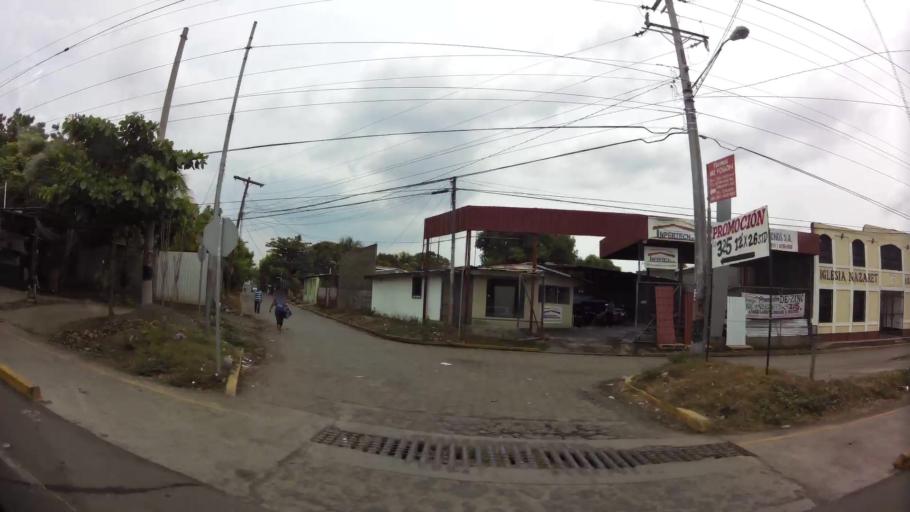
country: NI
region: Leon
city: Leon
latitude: 12.4507
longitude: -86.8636
